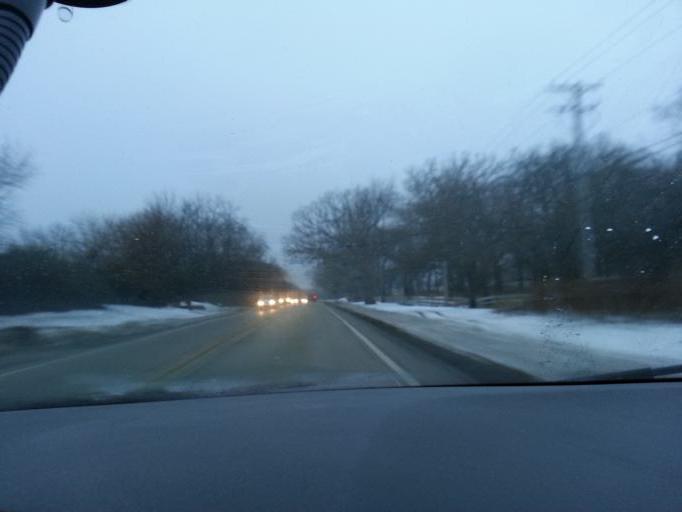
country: US
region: Illinois
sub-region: Kane County
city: Carpentersville
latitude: 42.1338
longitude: -88.2314
